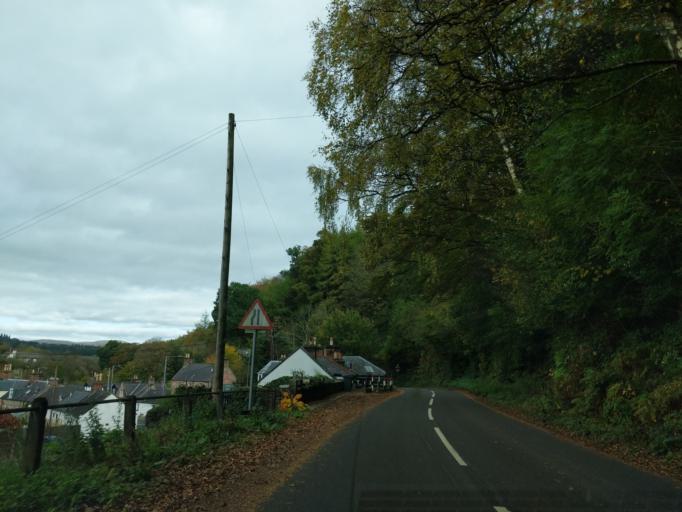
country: GB
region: Scotland
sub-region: Dumfries and Galloway
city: Thornhill
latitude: 55.2629
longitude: -3.7799
